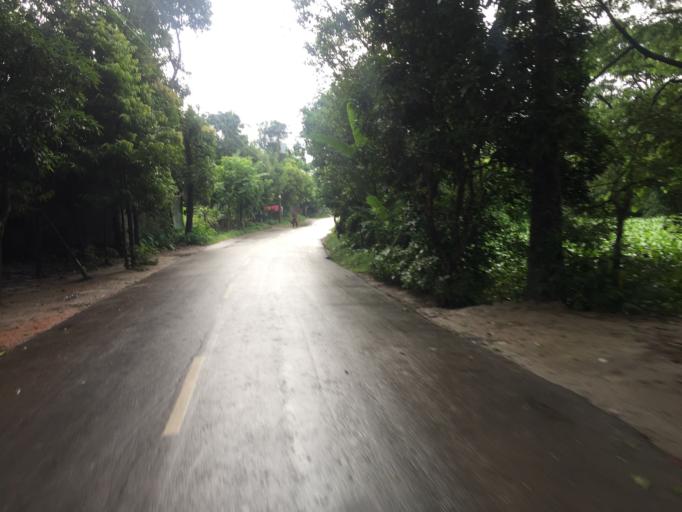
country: BD
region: Dhaka
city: Narayanganj
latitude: 23.5458
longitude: 90.4827
